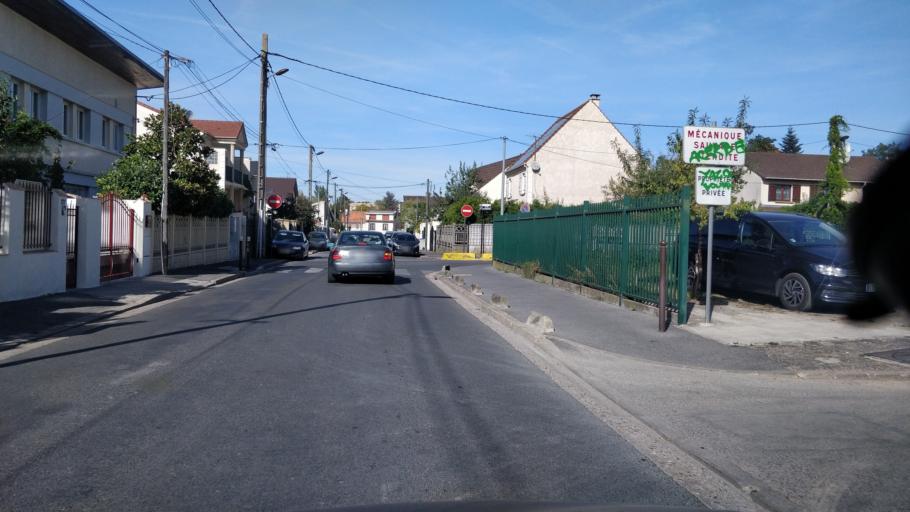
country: FR
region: Ile-de-France
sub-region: Departement de Seine-Saint-Denis
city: Livry-Gargan
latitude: 48.9114
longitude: 2.5385
